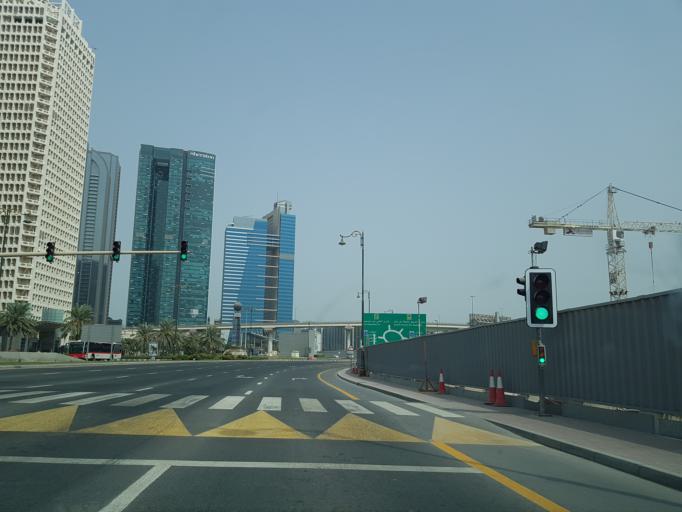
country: AE
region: Ash Shariqah
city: Sharjah
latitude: 25.2269
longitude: 55.2911
